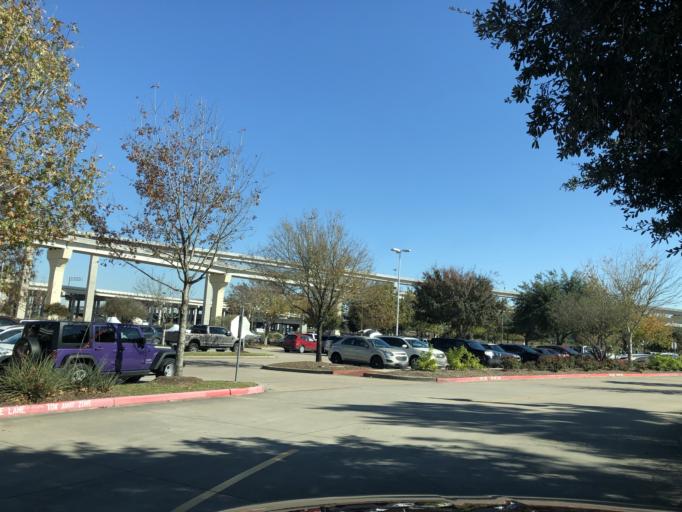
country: US
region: Texas
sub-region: Brazoria County
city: Brookside Village
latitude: 29.5956
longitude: -95.3900
